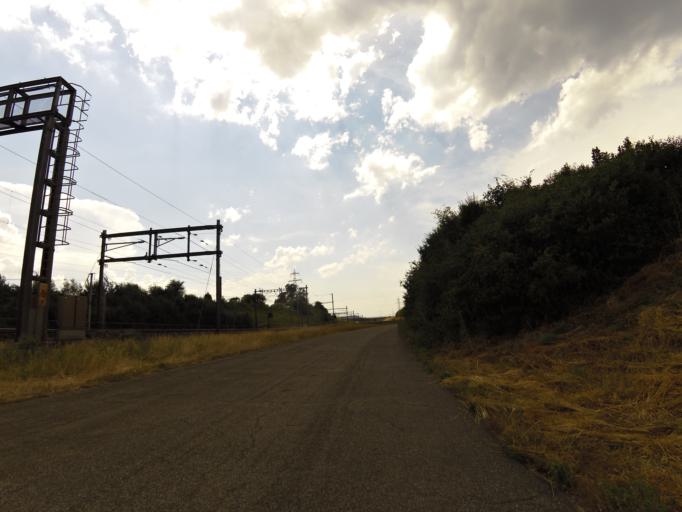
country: CH
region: Aargau
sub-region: Bezirk Lenzburg
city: Othmarsingen
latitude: 47.3938
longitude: 8.1999
